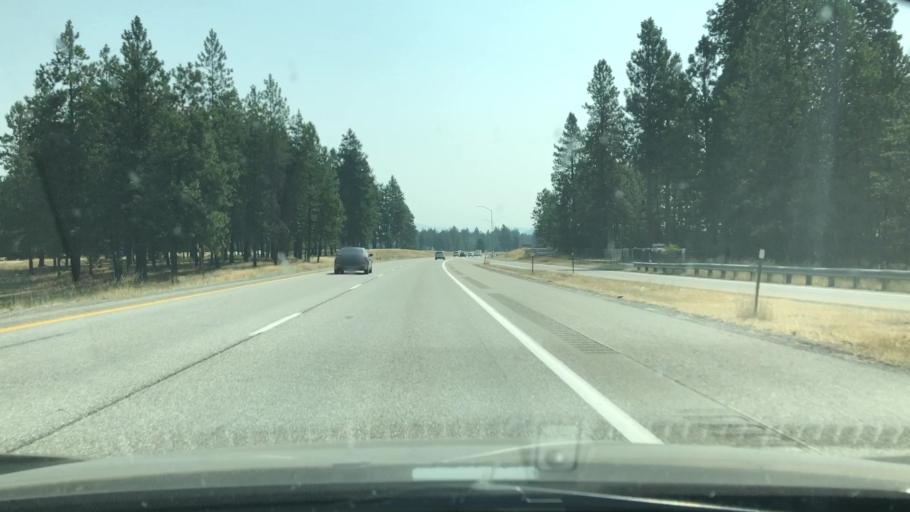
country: US
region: Idaho
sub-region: Kootenai County
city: Coeur d'Alene
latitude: 47.7084
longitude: -116.8606
